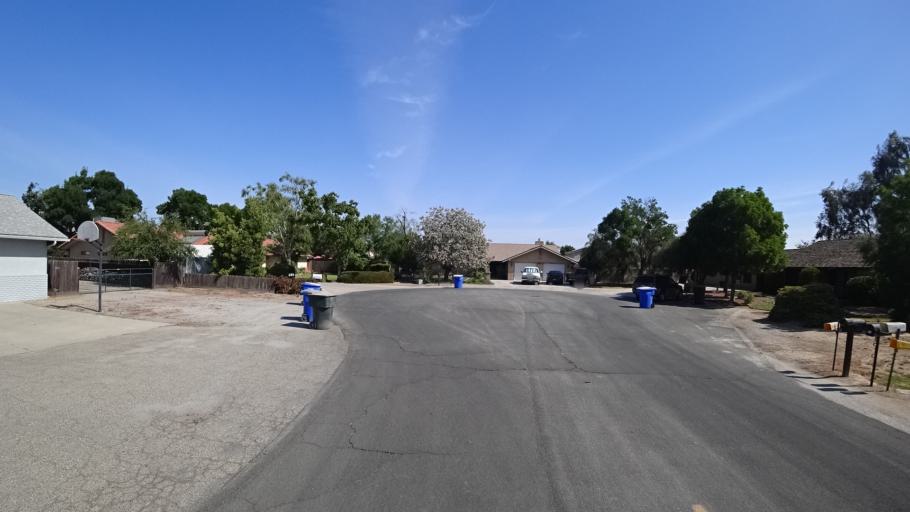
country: US
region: California
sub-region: Kings County
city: Hanford
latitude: 36.3493
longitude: -119.6657
